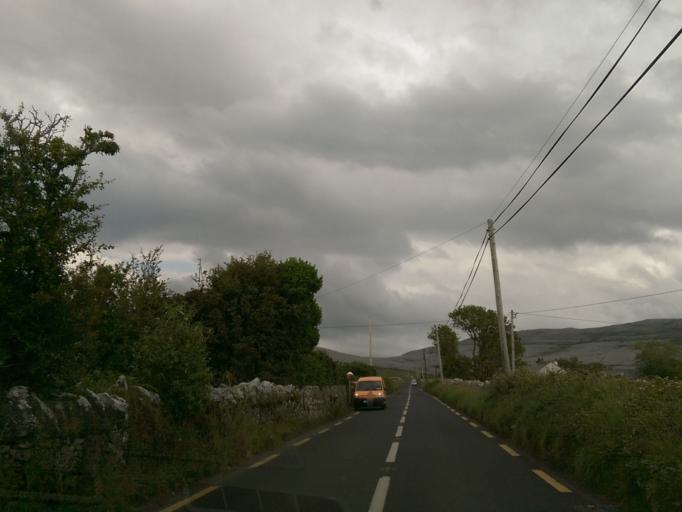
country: IE
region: Connaught
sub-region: County Galway
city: Bearna
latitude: 53.1214
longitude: -9.1337
